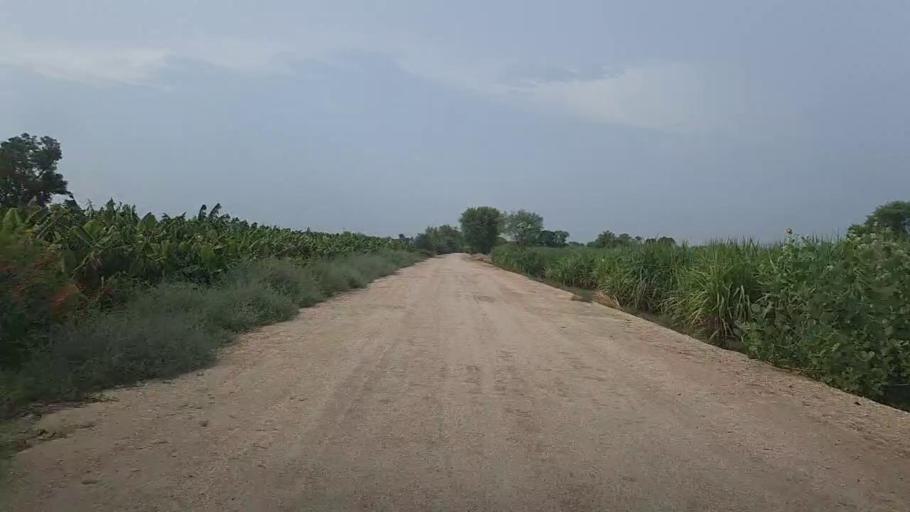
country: PK
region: Sindh
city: Karaundi
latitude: 26.9810
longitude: 68.4339
